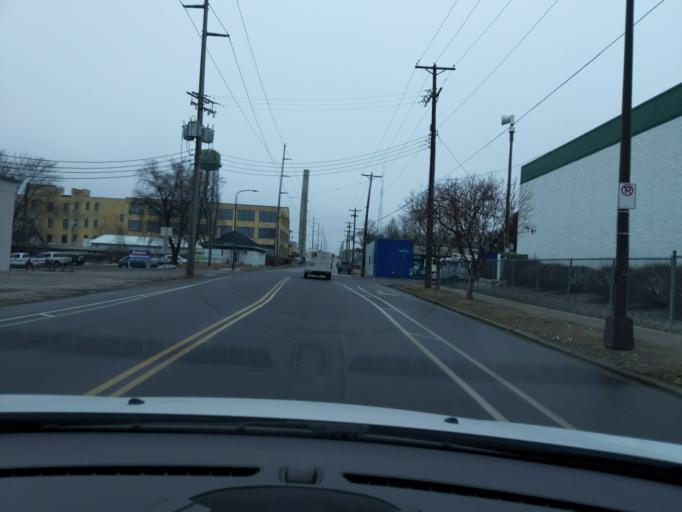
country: US
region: Minnesota
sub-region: Ramsey County
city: Falcon Heights
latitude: 44.9624
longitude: -93.1823
